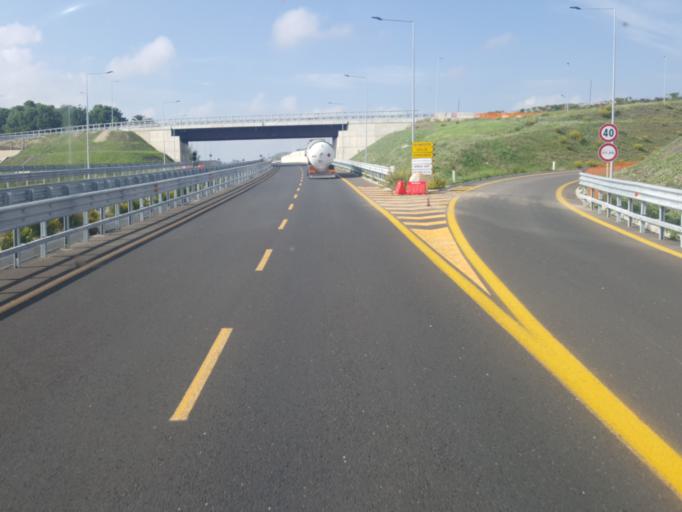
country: IT
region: Sicily
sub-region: Provincia di Caltanissetta
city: Serradifalco
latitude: 37.4215
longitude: 13.9122
